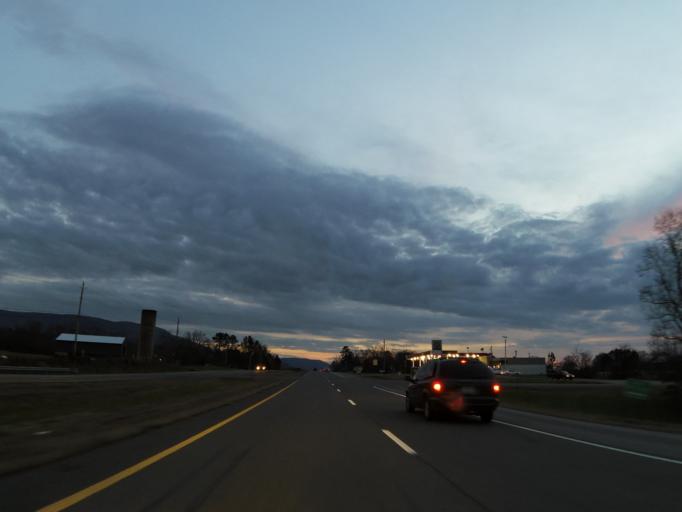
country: US
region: Tennessee
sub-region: McMinn County
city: Etowah
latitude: 35.2630
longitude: -84.5500
